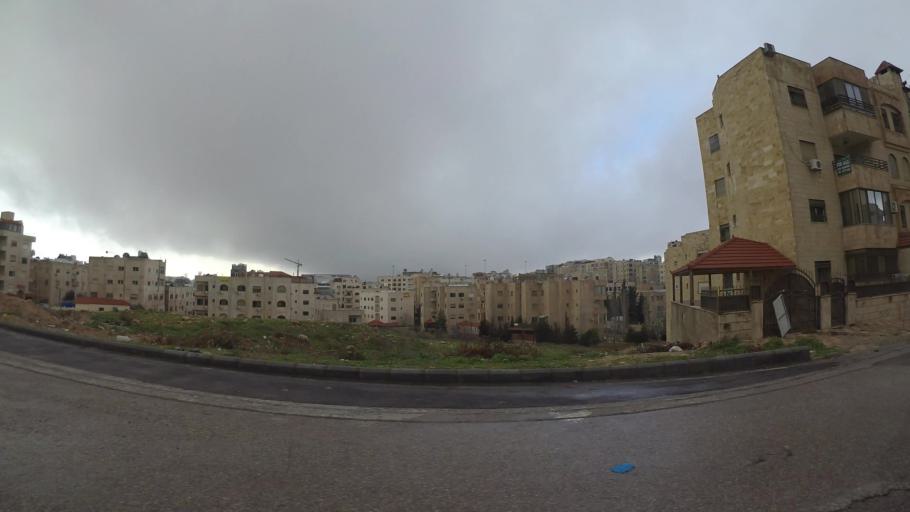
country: JO
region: Amman
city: Wadi as Sir
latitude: 31.9436
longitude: 35.8554
